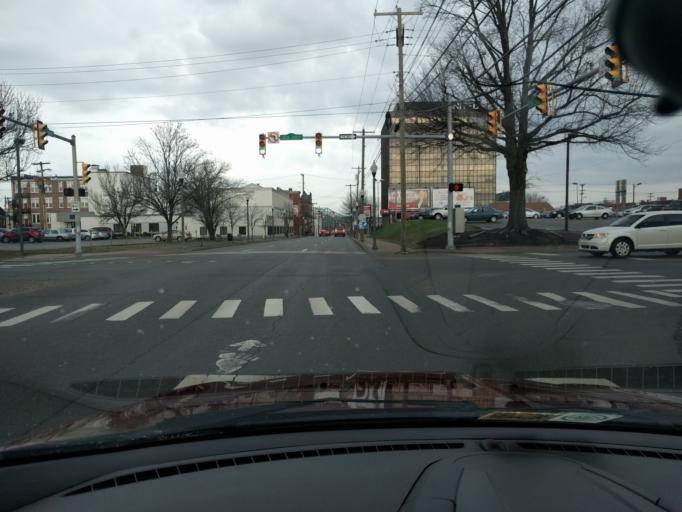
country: US
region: West Virginia
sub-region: Wood County
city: Parkersburg
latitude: 39.2638
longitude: -81.5585
